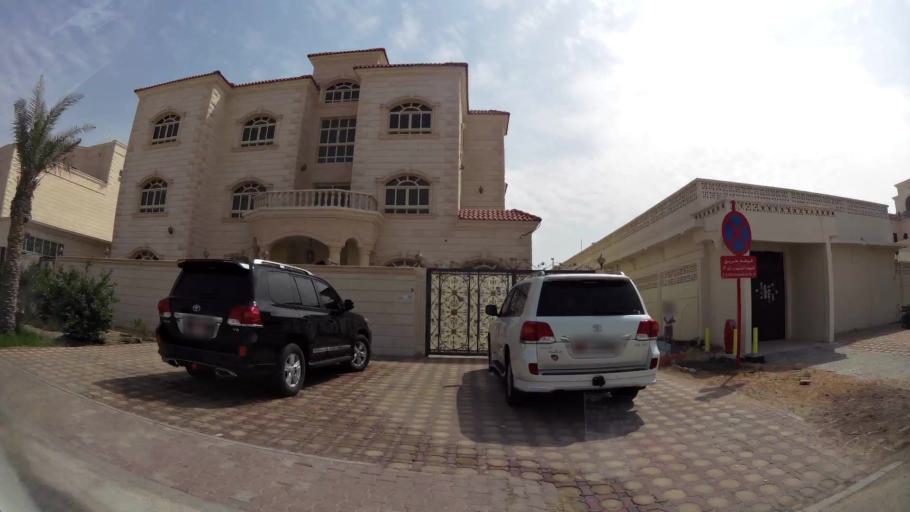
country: AE
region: Abu Dhabi
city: Abu Dhabi
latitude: 24.5438
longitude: 54.6823
